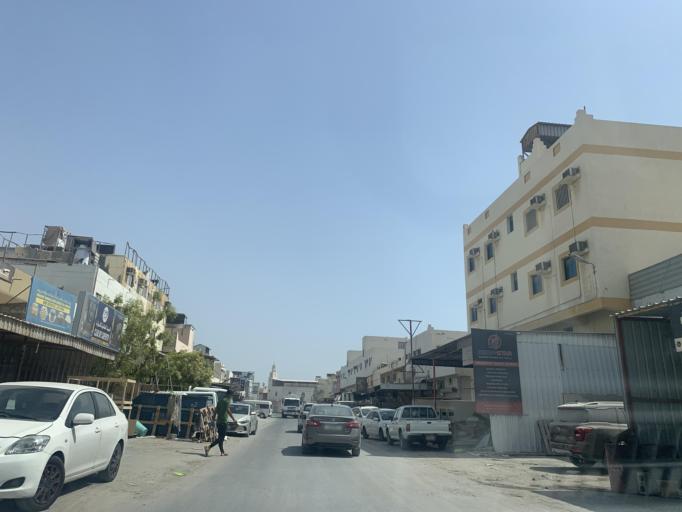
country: BH
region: Central Governorate
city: Madinat Hamad
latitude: 26.1392
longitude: 50.4844
